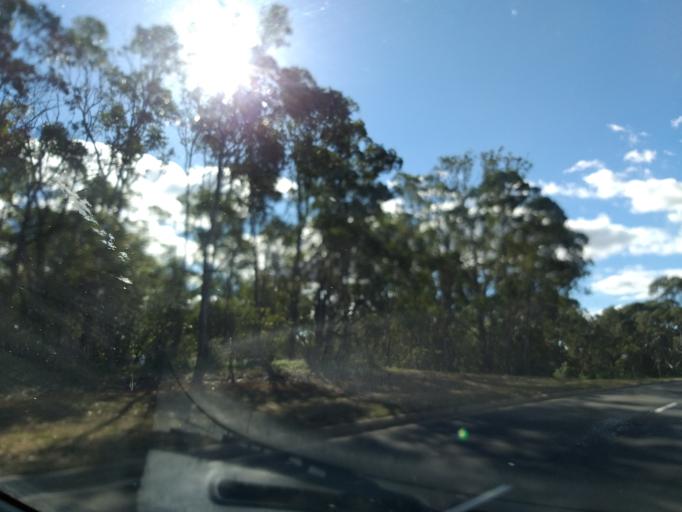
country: AU
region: New South Wales
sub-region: Shellharbour
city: Albion Park Rail
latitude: -34.5674
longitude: 150.8246
